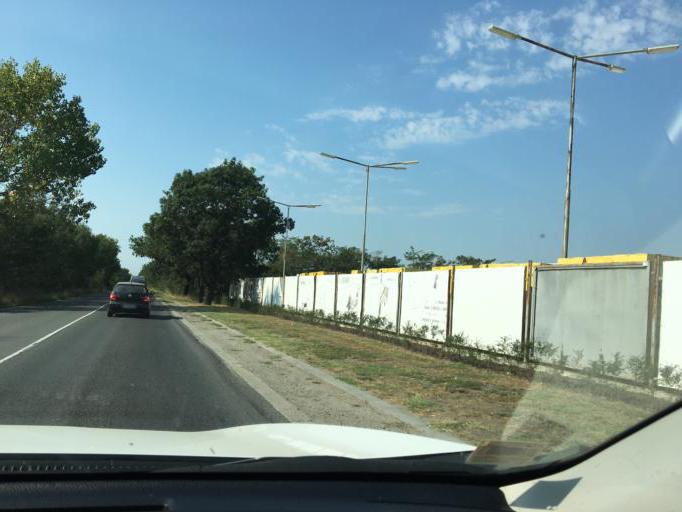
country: BG
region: Burgas
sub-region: Obshtina Burgas
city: Burgas
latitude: 42.5613
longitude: 27.4933
